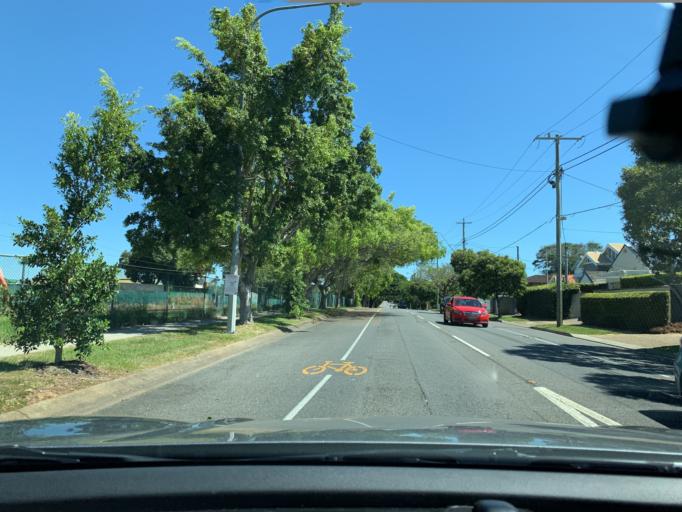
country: AU
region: Queensland
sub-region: Brisbane
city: Ascot
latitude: -27.4253
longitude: 153.0630
